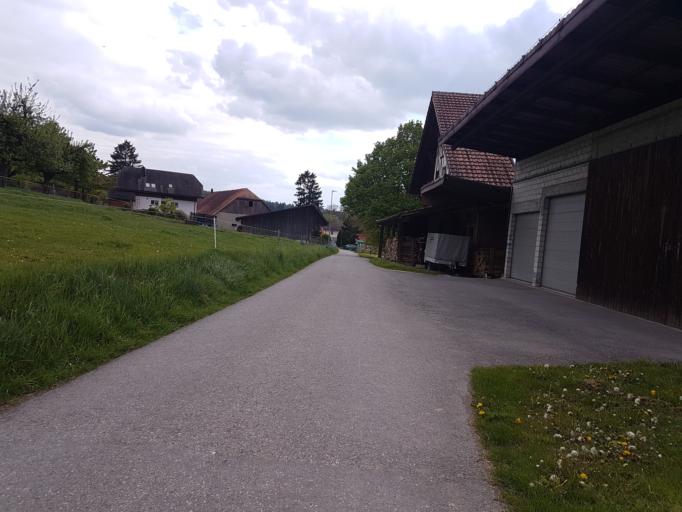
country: CH
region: Bern
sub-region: Seeland District
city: Arch
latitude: 47.1530
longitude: 7.4097
